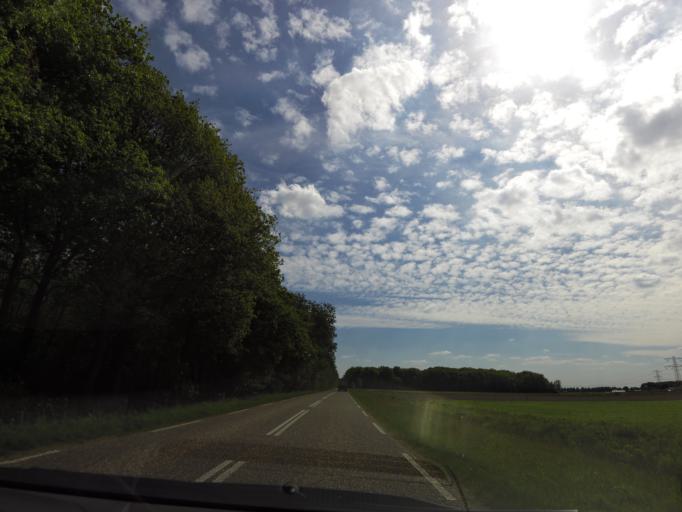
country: NL
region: Limburg
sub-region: Gemeente Leudal
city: Haelen
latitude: 51.2807
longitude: 5.9788
